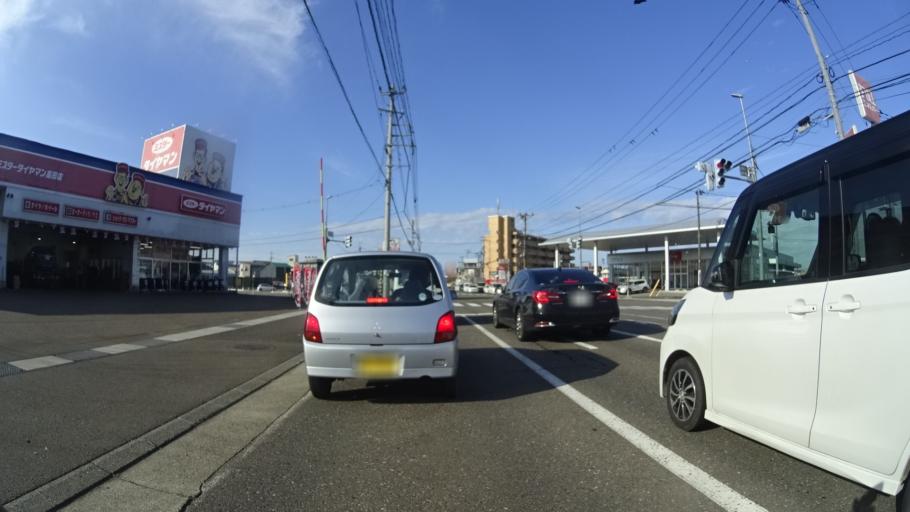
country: JP
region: Niigata
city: Joetsu
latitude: 37.1245
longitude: 138.2502
